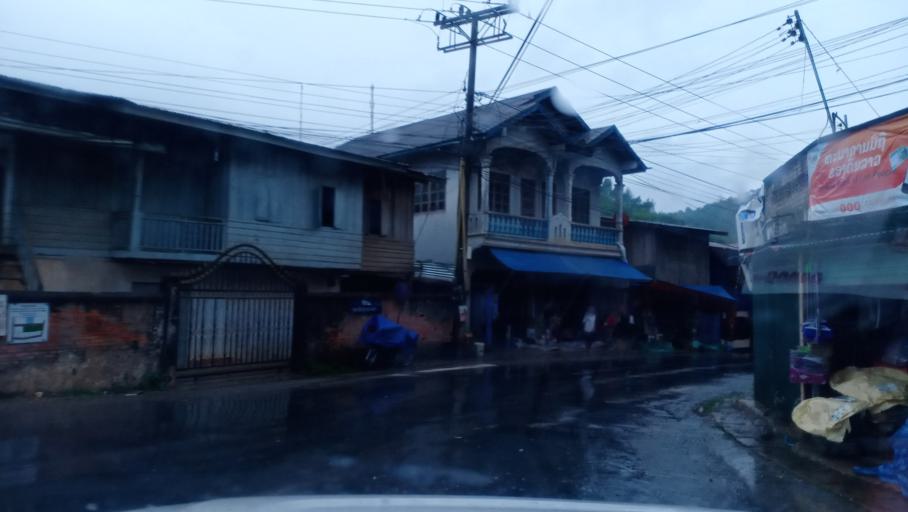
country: LA
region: Phongsali
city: Khoa
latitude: 21.0808
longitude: 102.5054
